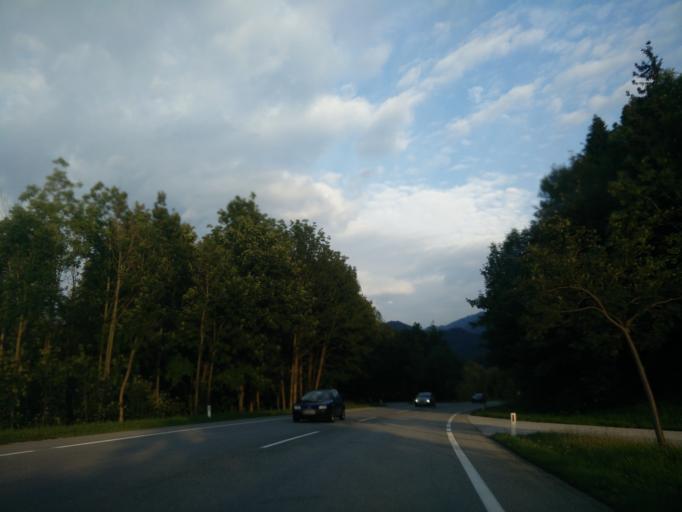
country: AT
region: Salzburg
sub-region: Politischer Bezirk Salzburg-Umgebung
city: Fuschl am See
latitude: 47.7950
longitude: 13.2817
